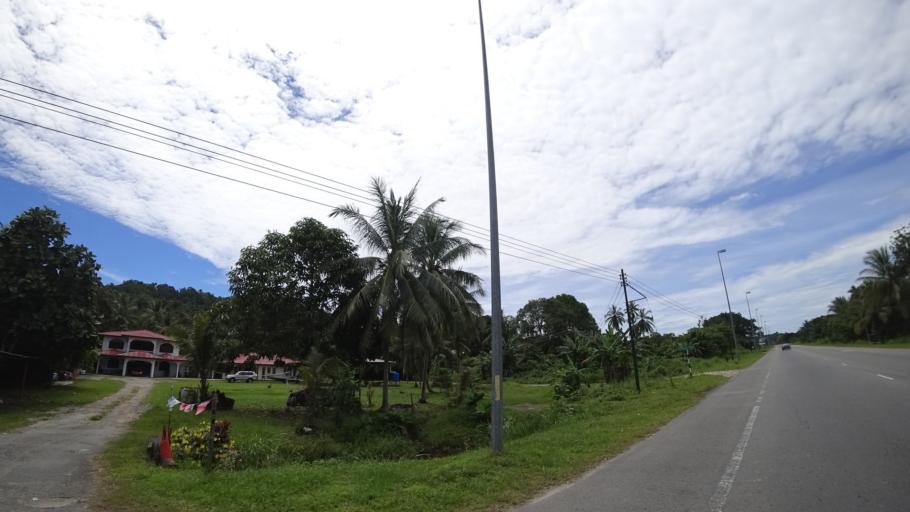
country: BN
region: Tutong
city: Tutong
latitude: 4.7817
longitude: 114.8205
